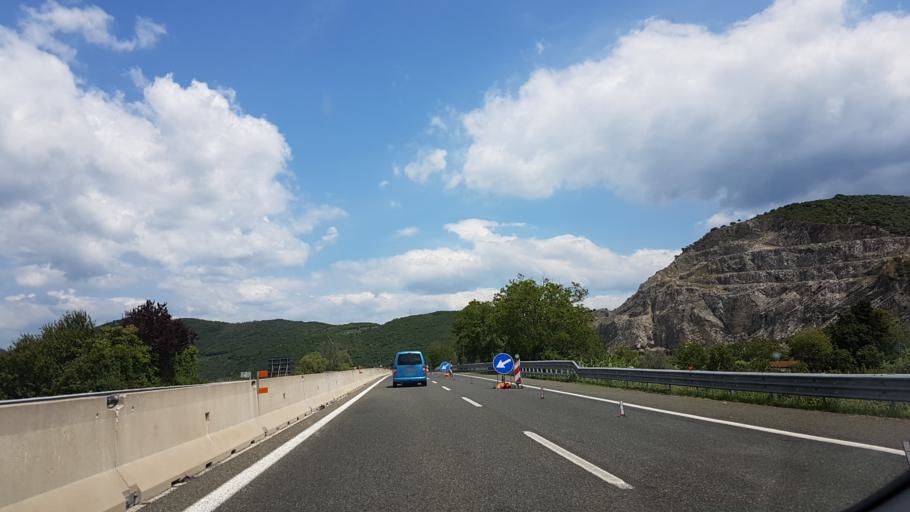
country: IT
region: Tuscany
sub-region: Province of Pisa
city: Vecchiano-Nodica
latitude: 43.8011
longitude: 10.3654
